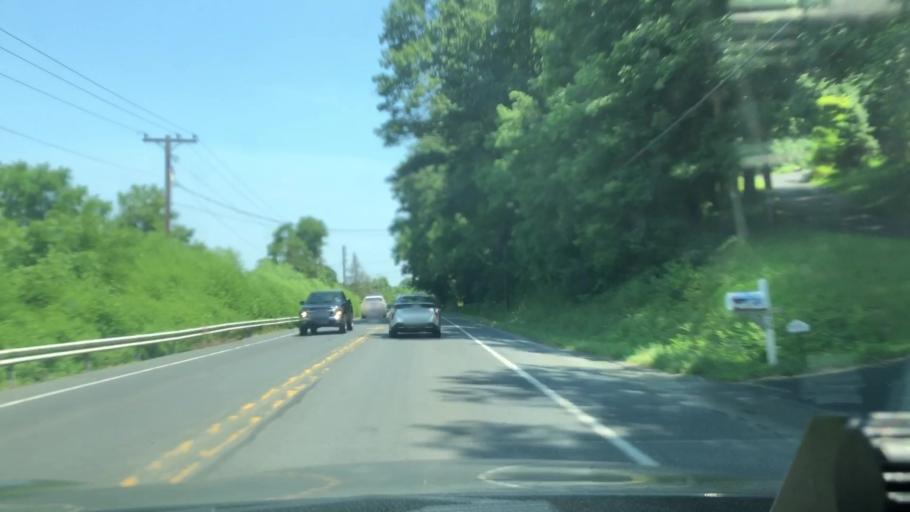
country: US
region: Pennsylvania
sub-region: Berks County
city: New Berlinville
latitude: 40.3650
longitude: -75.6252
